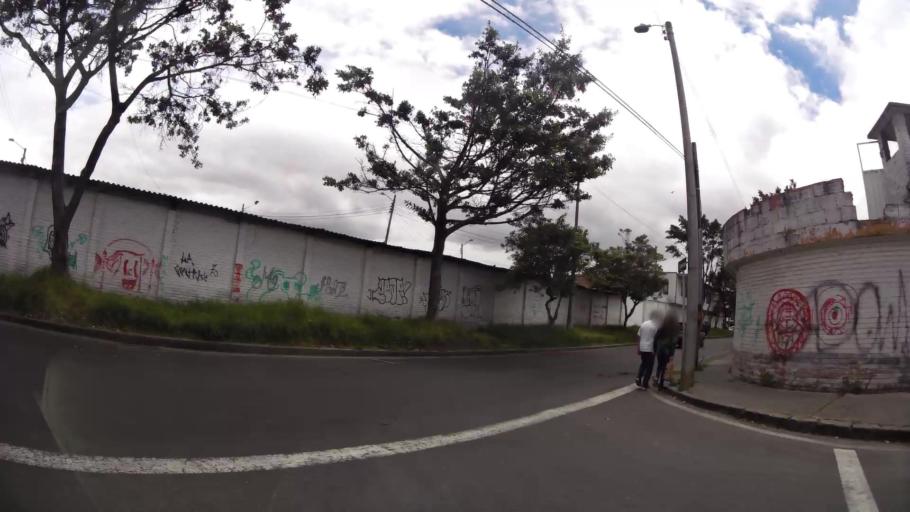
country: CO
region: Bogota D.C.
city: Bogota
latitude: 4.6058
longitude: -74.1056
